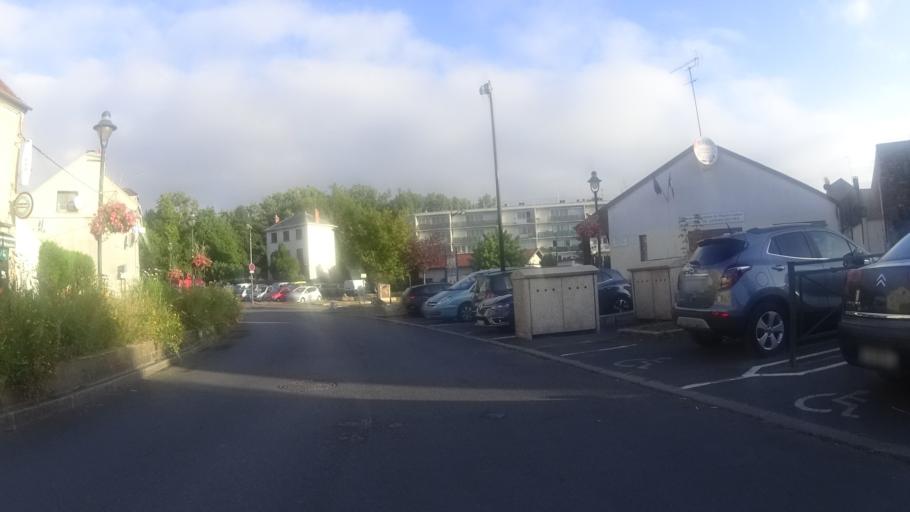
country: FR
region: Ile-de-France
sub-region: Departement de l'Essonne
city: Villabe
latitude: 48.5856
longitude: 2.4706
